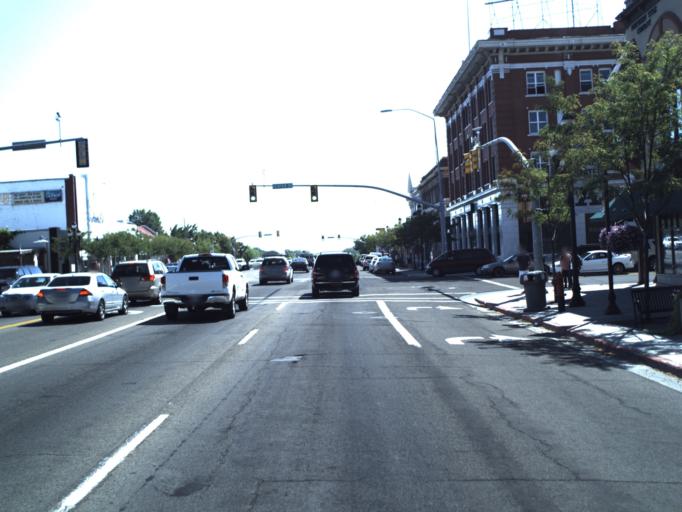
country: US
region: Utah
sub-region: Cache County
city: Logan
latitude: 41.7318
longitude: -111.8351
